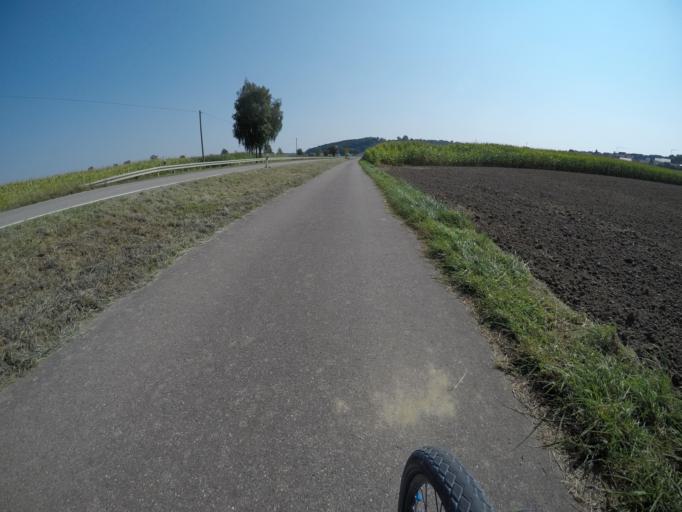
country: DE
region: Bavaria
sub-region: Swabia
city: Aislingen
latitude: 48.5097
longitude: 10.4459
